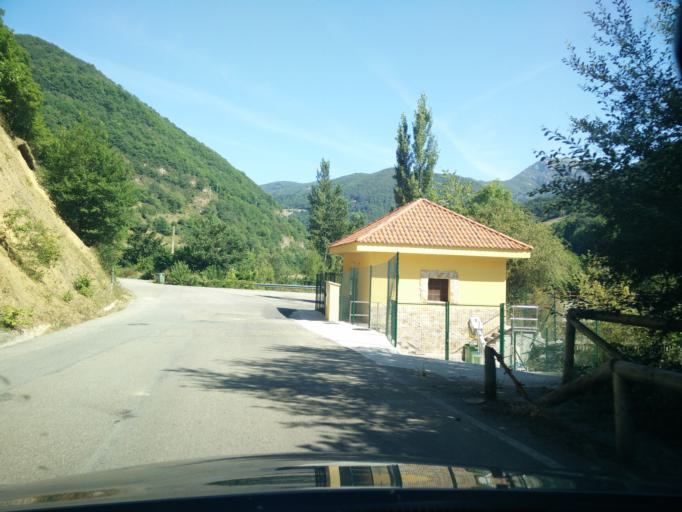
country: ES
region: Asturias
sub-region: Province of Asturias
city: Campo de Caso
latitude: 43.1916
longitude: -5.3831
